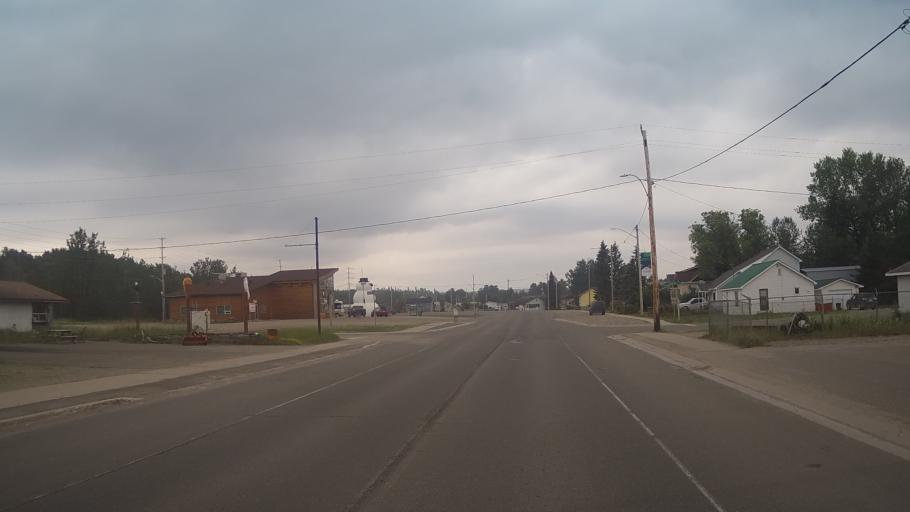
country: CA
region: Ontario
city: Greenstone
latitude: 49.6008
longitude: -87.9600
